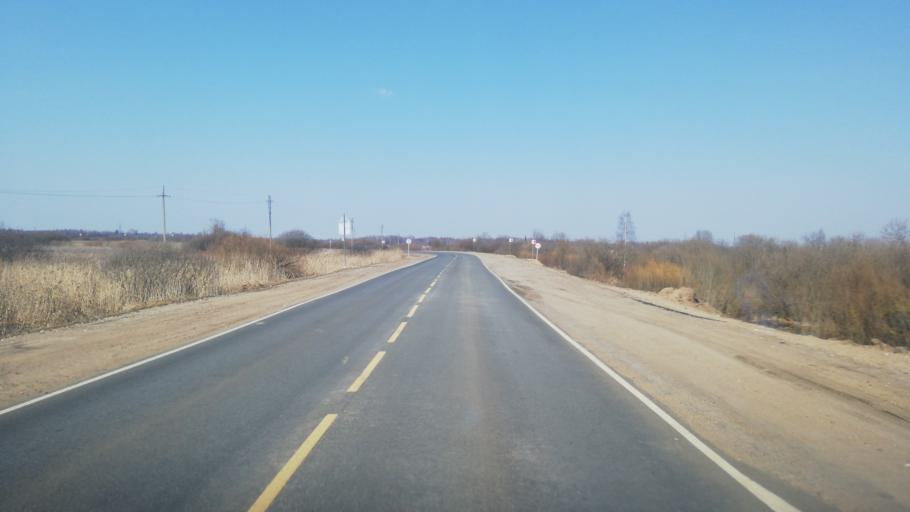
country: RU
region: Jaroslavl
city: Semibratovo
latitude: 57.2266
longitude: 39.5153
